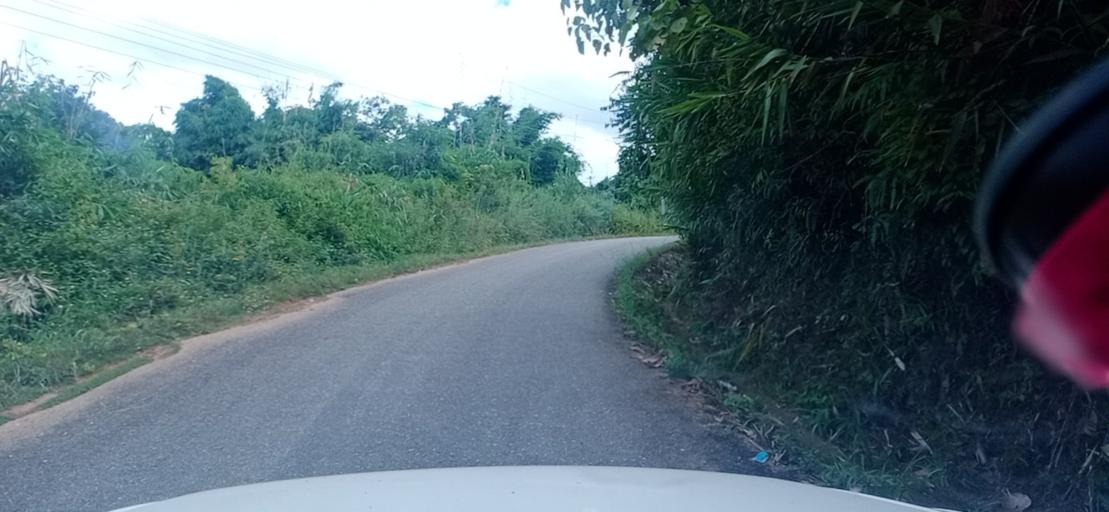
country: TH
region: Changwat Bueng Kan
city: Pak Khat
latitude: 18.6697
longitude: 103.1061
